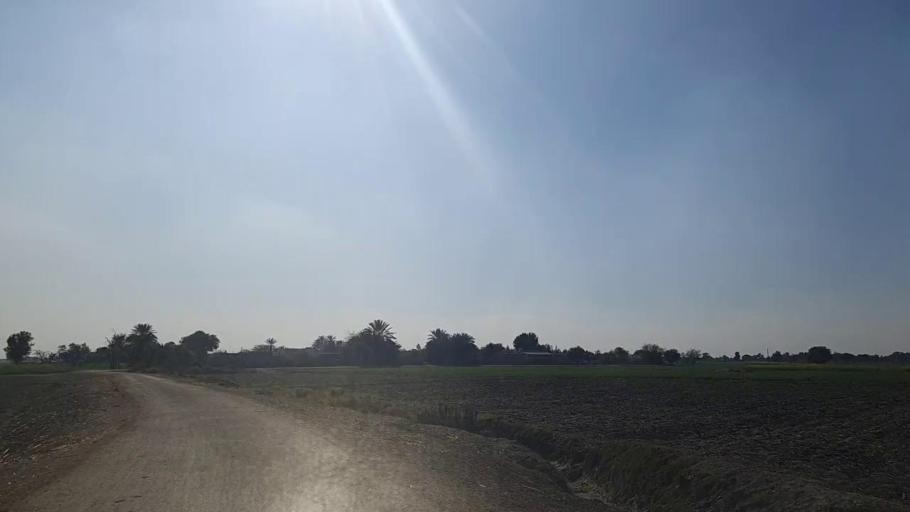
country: PK
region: Sindh
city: Shahpur Chakar
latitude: 26.2187
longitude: 68.6031
